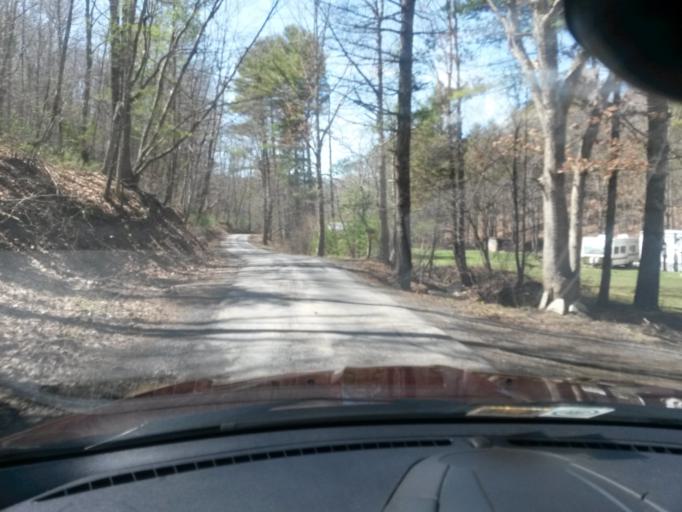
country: US
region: West Virginia
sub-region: Greenbrier County
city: White Sulphur Springs
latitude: 37.6813
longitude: -80.3348
